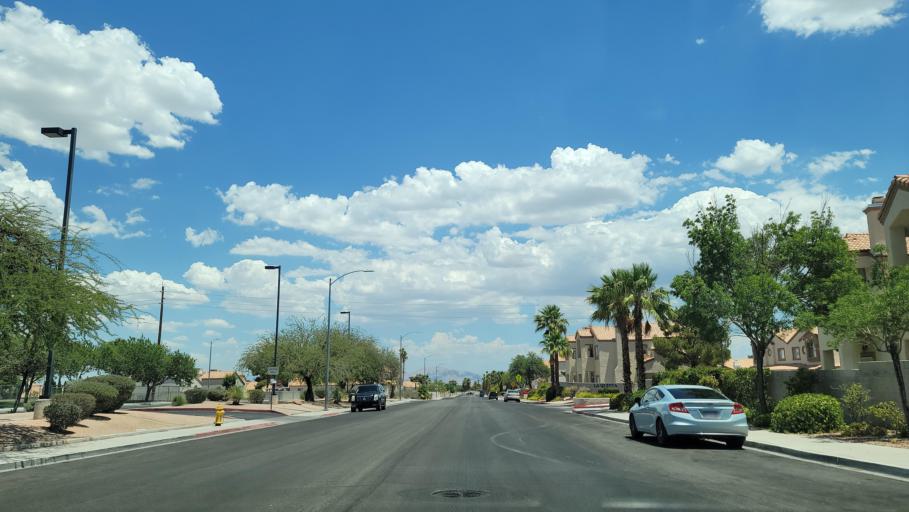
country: US
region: Nevada
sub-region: Clark County
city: Spring Valley
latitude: 36.1627
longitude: -115.2748
